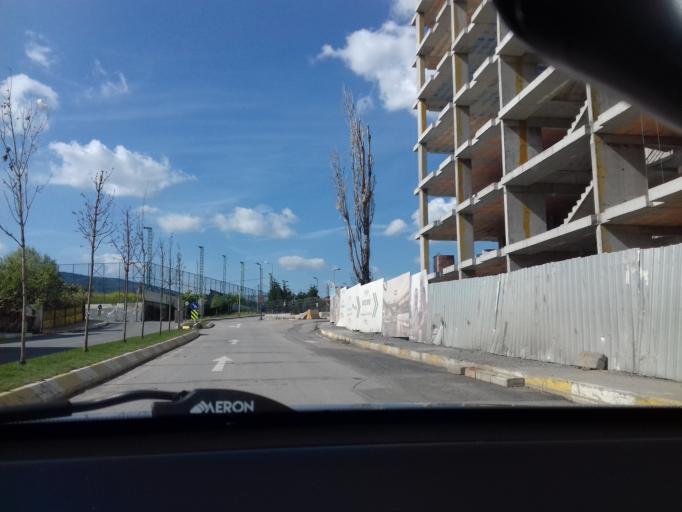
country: TR
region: Istanbul
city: Pendik
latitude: 40.8978
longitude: 29.2775
